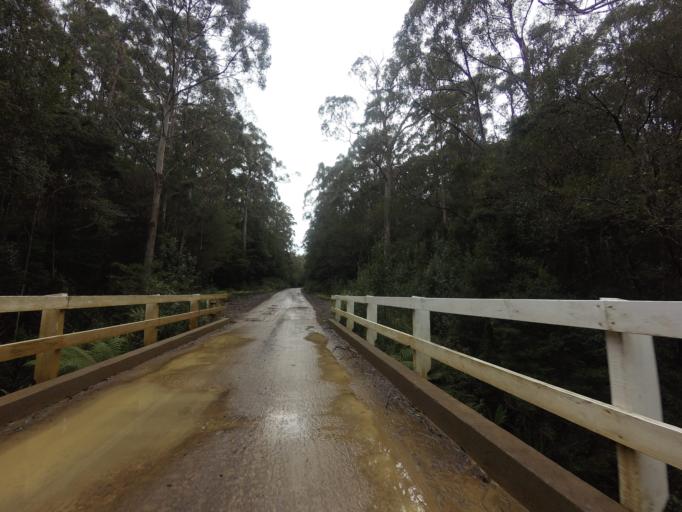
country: AU
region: Tasmania
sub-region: Huon Valley
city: Geeveston
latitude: -43.5068
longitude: 146.8758
